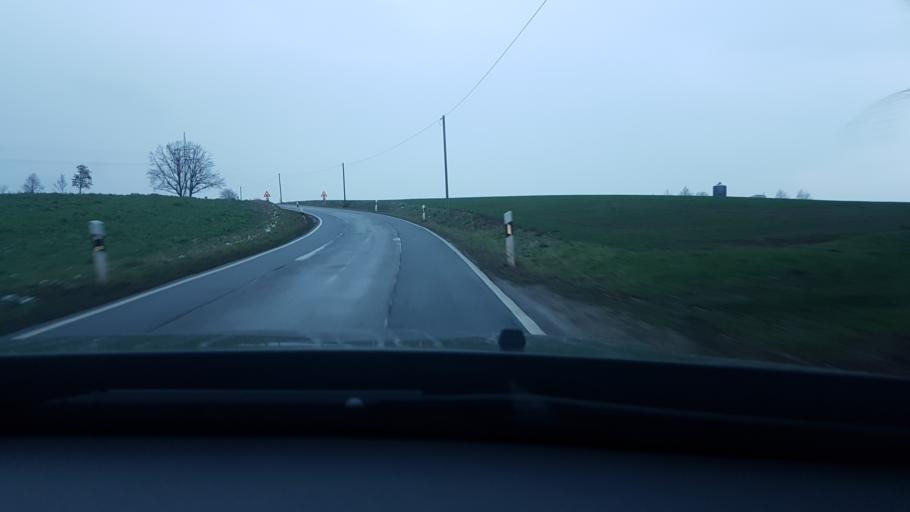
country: DE
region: Hesse
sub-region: Regierungsbezirk Kassel
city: Korbach
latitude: 51.3244
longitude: 8.9088
